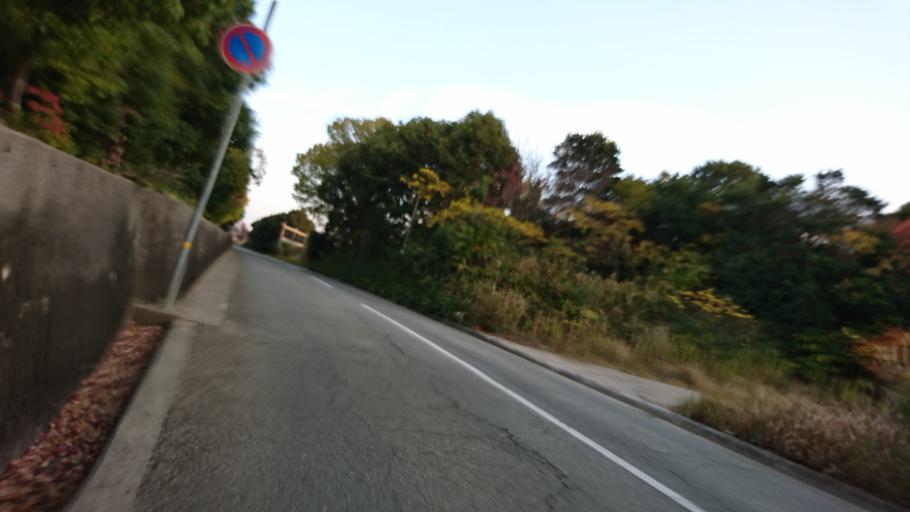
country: JP
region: Hyogo
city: Kakogawacho-honmachi
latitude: 34.7754
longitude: 134.8624
